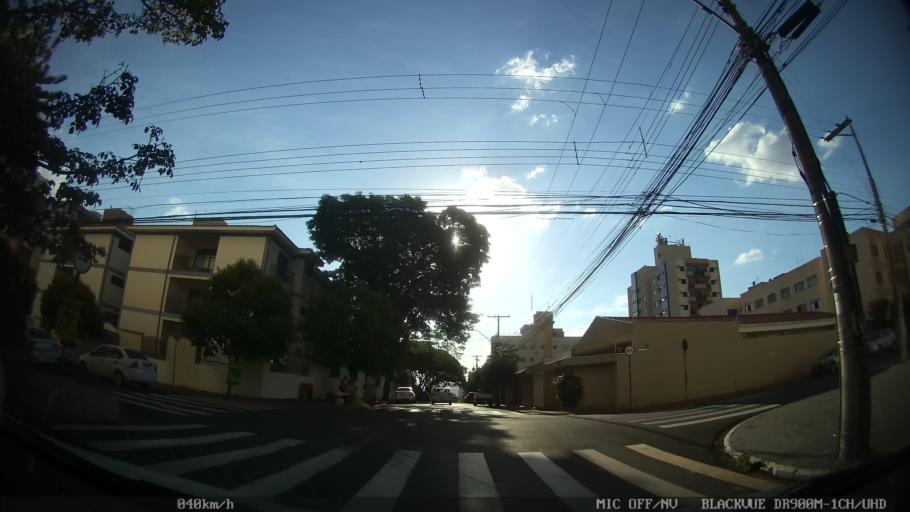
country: BR
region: Sao Paulo
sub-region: Ribeirao Preto
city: Ribeirao Preto
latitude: -21.1844
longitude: -47.7888
